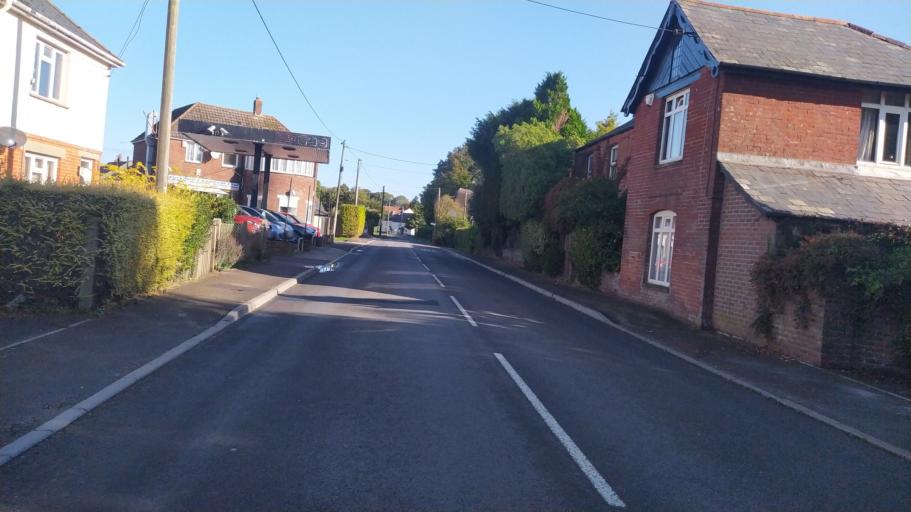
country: GB
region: England
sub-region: Dorset
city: Bovington Camp
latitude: 50.7777
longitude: -2.1977
